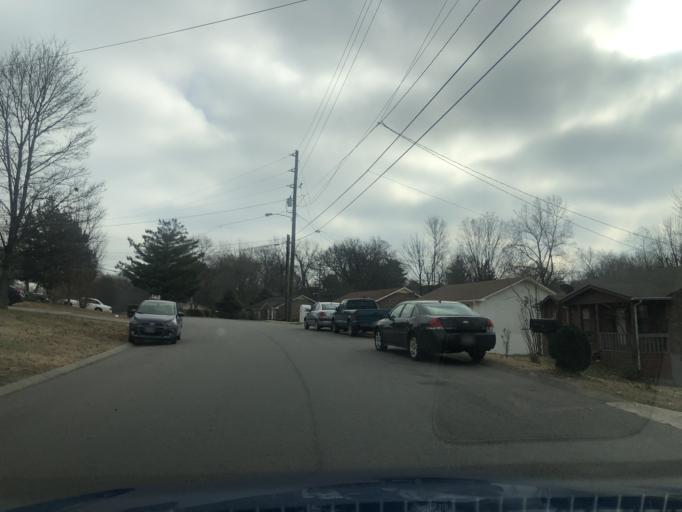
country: US
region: Tennessee
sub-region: Davidson County
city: Oak Hill
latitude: 36.0909
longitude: -86.7144
